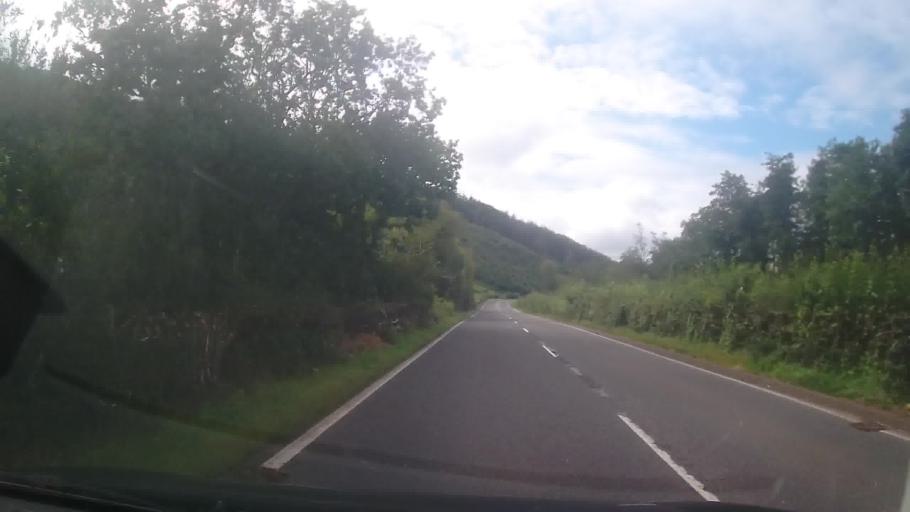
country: GB
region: Wales
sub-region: Sir Powys
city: Machynlleth
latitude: 52.5605
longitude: -3.9144
